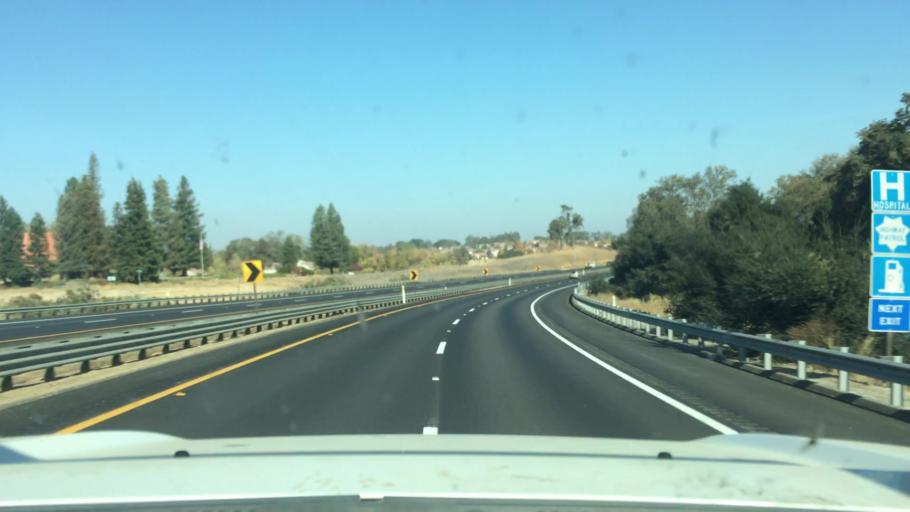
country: US
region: California
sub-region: San Luis Obispo County
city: Templeton
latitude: 35.5590
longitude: -120.7118
